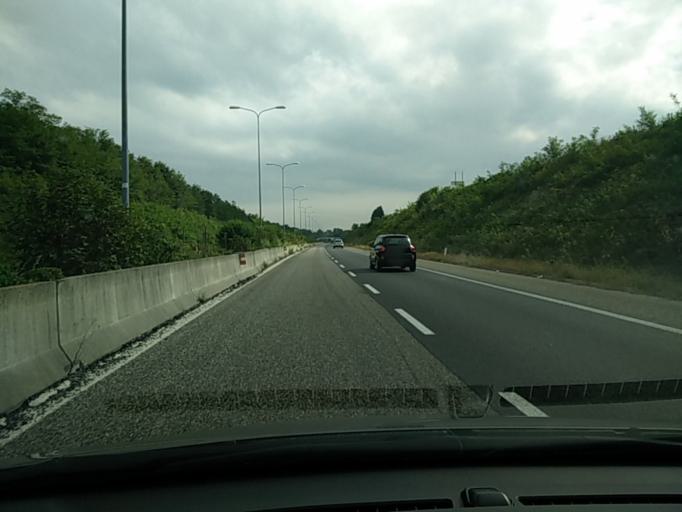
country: IT
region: Lombardy
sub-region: Provincia di Varese
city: Vizzola Ticino
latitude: 45.6001
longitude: 8.7129
